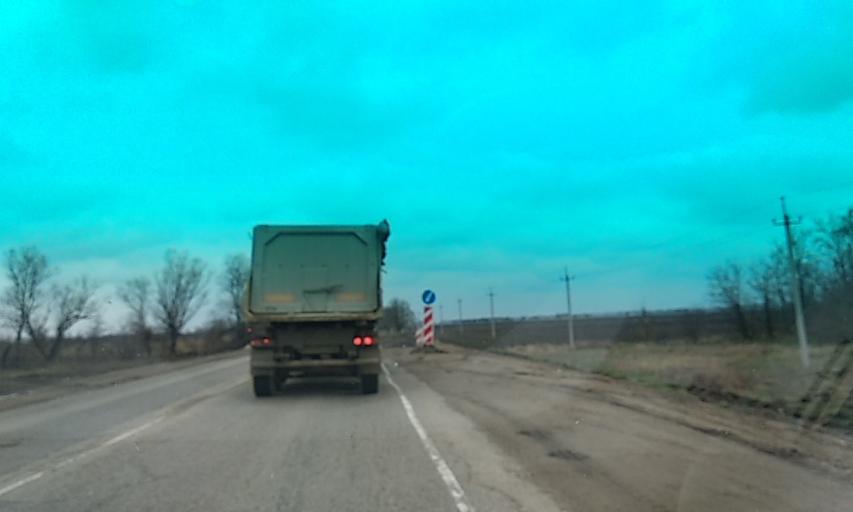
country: RU
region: Adygeya
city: Beloye
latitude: 44.9974
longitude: 39.7095
